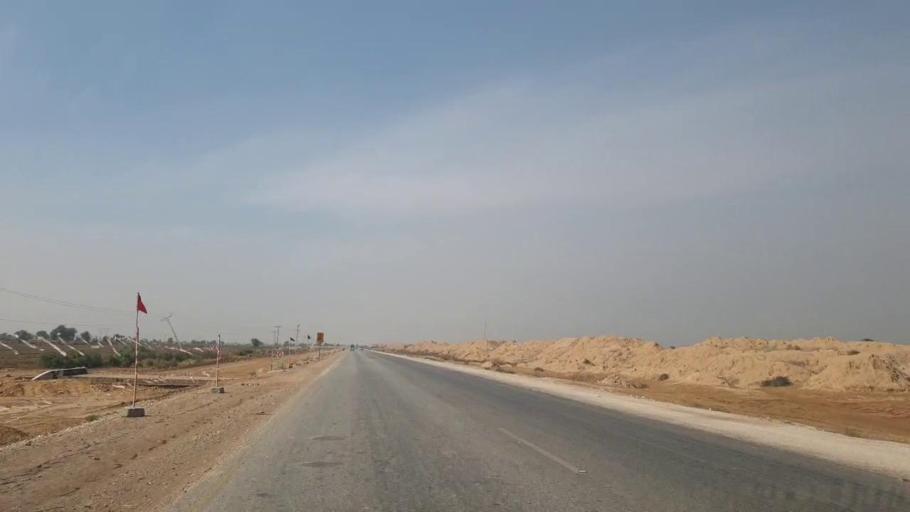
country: PK
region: Sindh
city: Sann
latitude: 26.0062
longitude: 68.1547
